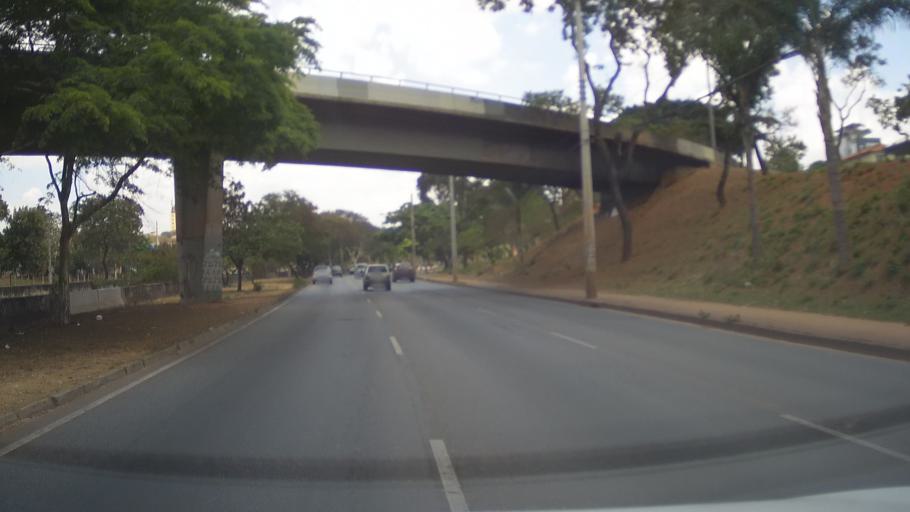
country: BR
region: Minas Gerais
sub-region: Belo Horizonte
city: Belo Horizonte
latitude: -19.9233
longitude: -43.9764
